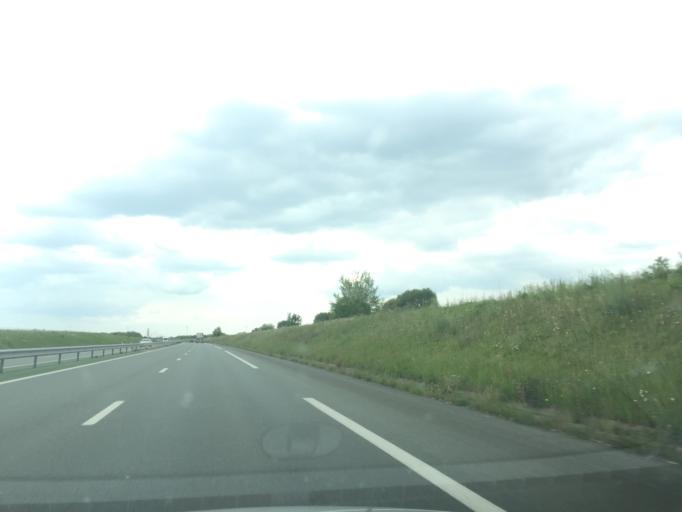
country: FR
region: Poitou-Charentes
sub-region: Departement des Deux-Sevres
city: Villiers-en-Plaine
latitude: 46.4182
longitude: -0.5606
